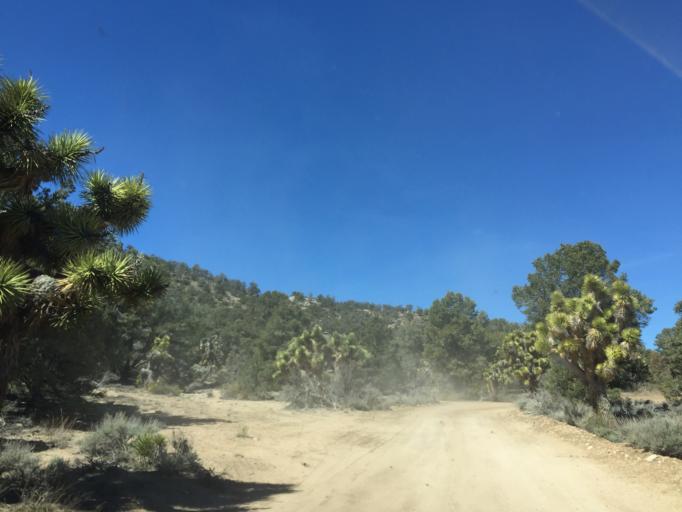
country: US
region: California
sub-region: San Bernardino County
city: Big Bear City
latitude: 34.2437
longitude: -116.7091
